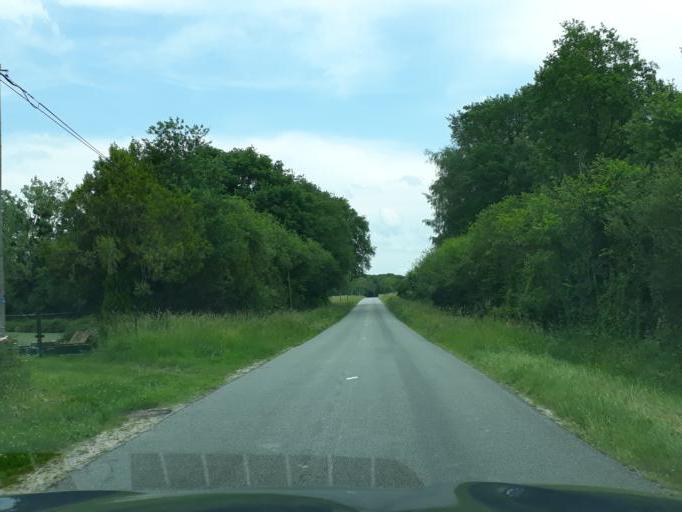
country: FR
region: Centre
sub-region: Departement du Loiret
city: Cerdon
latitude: 47.6886
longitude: 2.3429
